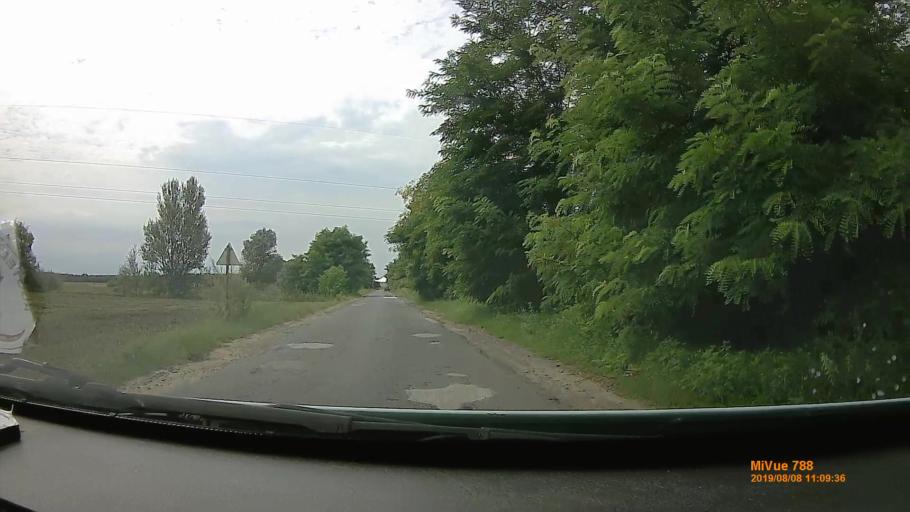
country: HU
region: Szabolcs-Szatmar-Bereg
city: Balkany
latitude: 47.7512
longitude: 21.8436
